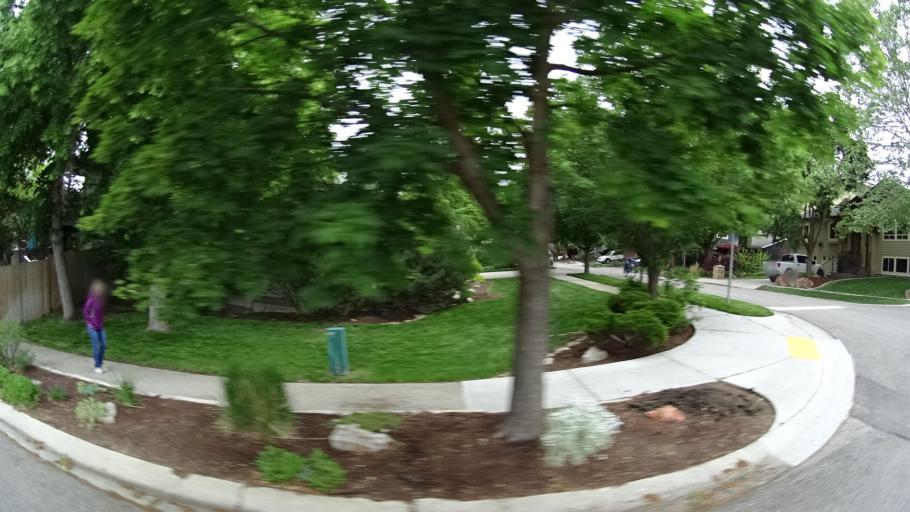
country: US
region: Idaho
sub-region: Ada County
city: Boise
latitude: 43.6120
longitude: -116.1739
